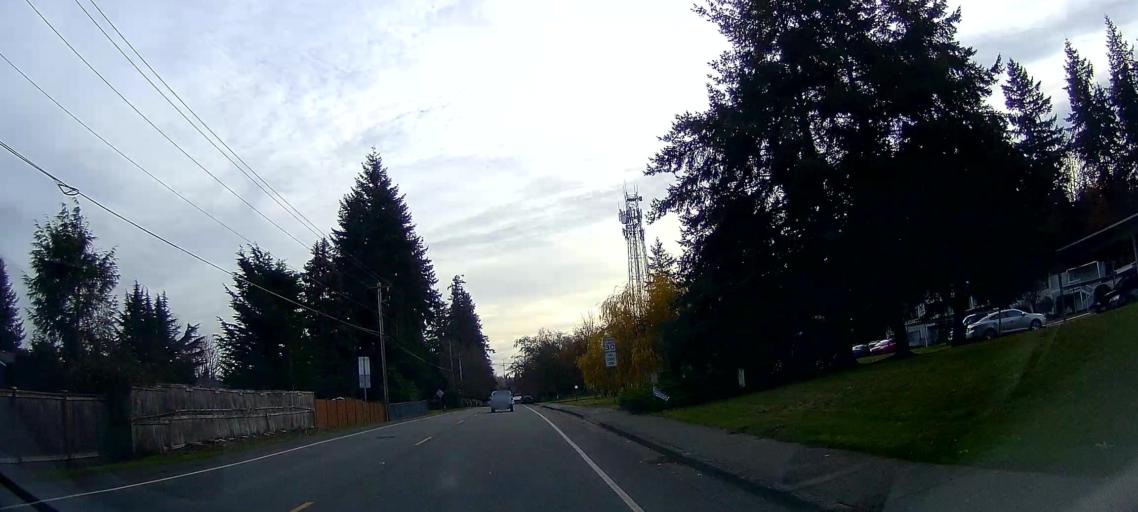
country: US
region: Washington
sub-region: Snohomish County
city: Brier
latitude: 47.7943
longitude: -122.2384
